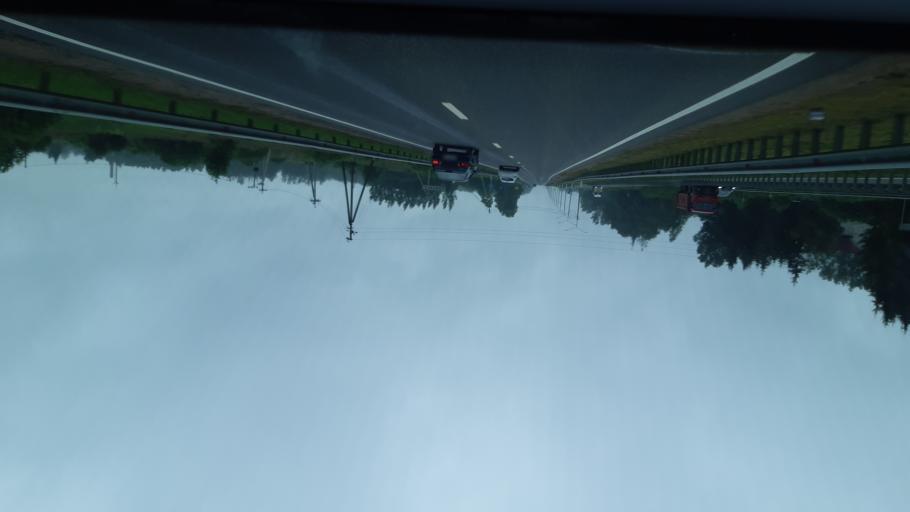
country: RU
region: Smolensk
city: Talashkino
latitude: 54.6692
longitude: 32.1511
